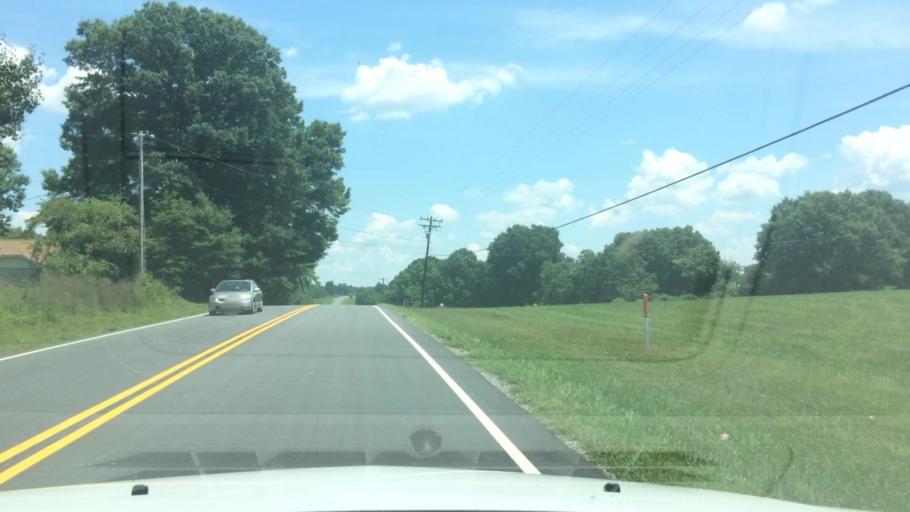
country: US
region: North Carolina
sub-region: Alexander County
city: Taylorsville
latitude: 35.9196
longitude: -81.2218
